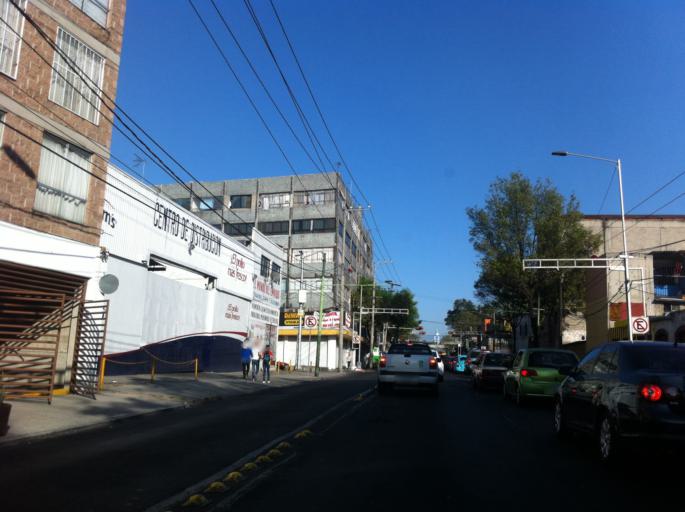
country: MX
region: Mexico City
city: Mexico City
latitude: 19.4136
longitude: -99.1254
